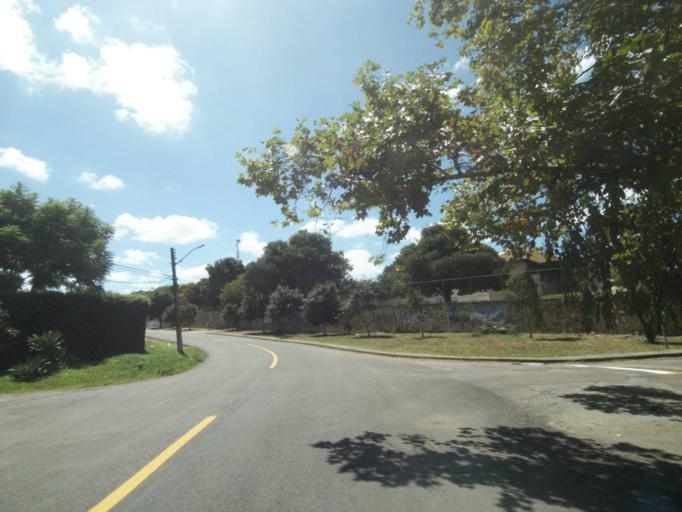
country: BR
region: Parana
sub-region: Pinhais
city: Pinhais
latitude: -25.4399
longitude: -49.2299
